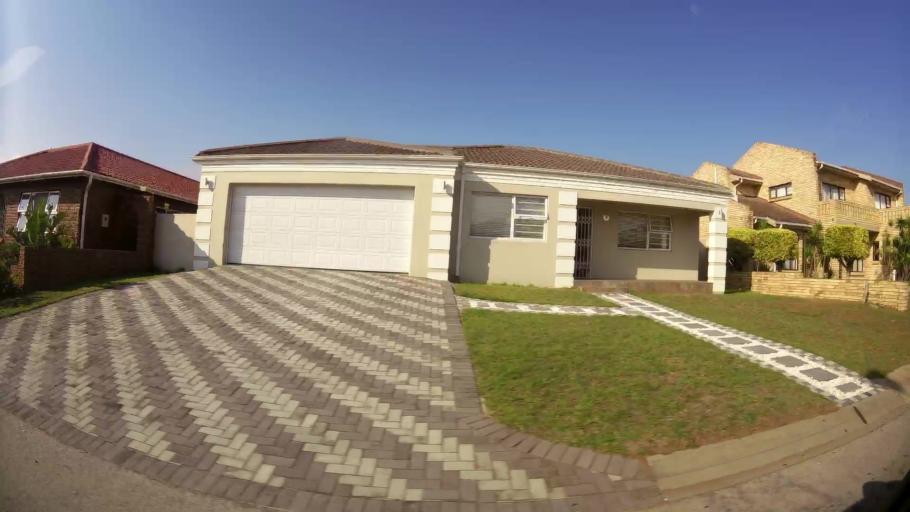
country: ZA
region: Eastern Cape
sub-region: Nelson Mandela Bay Metropolitan Municipality
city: Port Elizabeth
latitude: -33.9199
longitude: 25.5269
